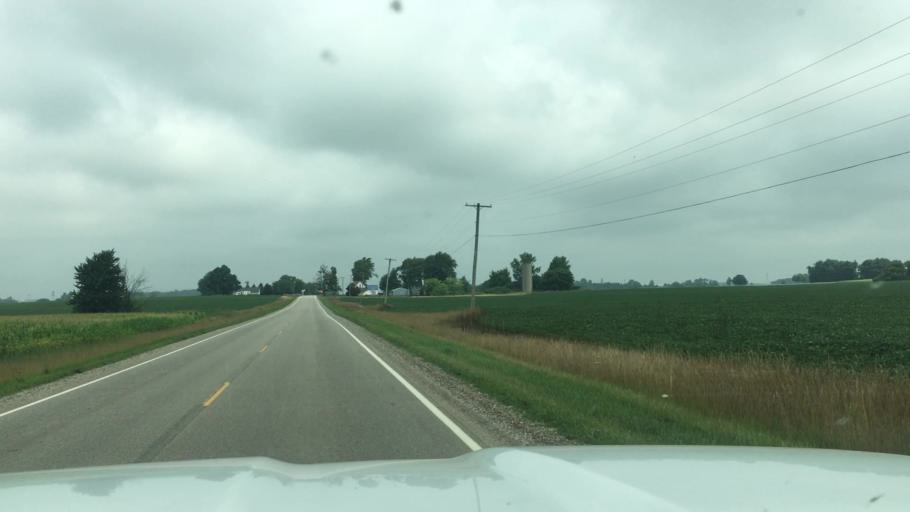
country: US
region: Michigan
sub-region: Sanilac County
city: Marlette
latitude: 43.3235
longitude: -82.9842
